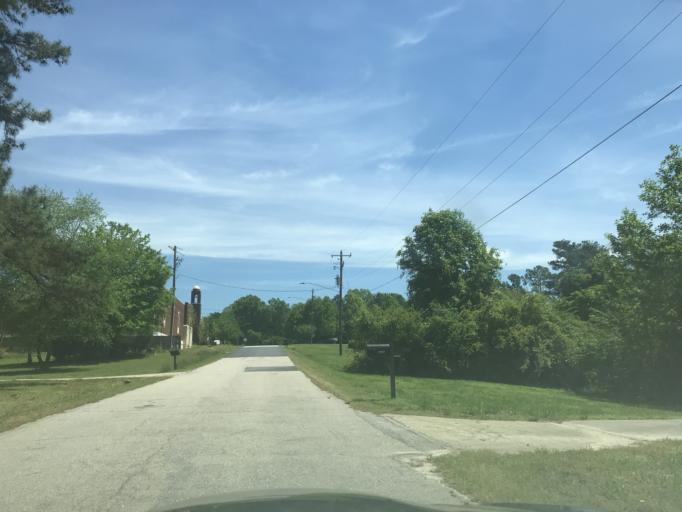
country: US
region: North Carolina
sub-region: Wake County
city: Raleigh
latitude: 35.8270
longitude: -78.5718
